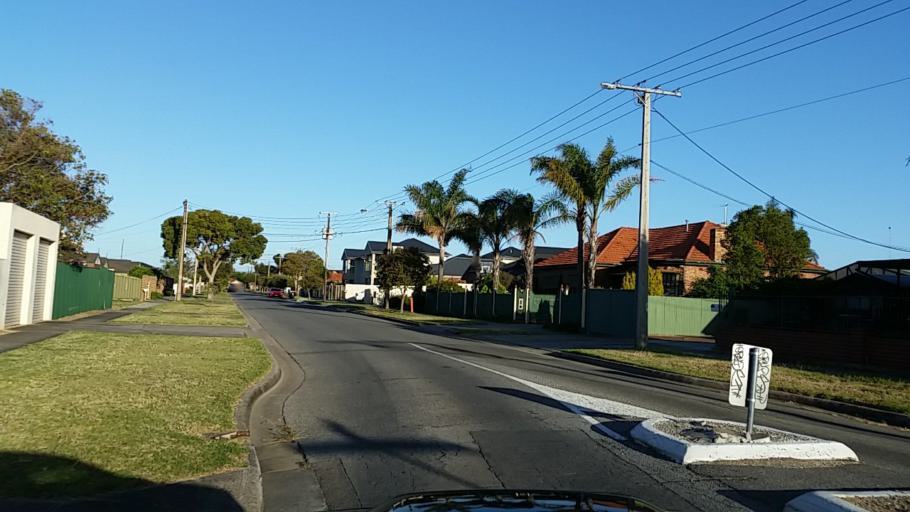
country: AU
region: South Australia
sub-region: Charles Sturt
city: Seaton
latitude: -34.8891
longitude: 138.5096
